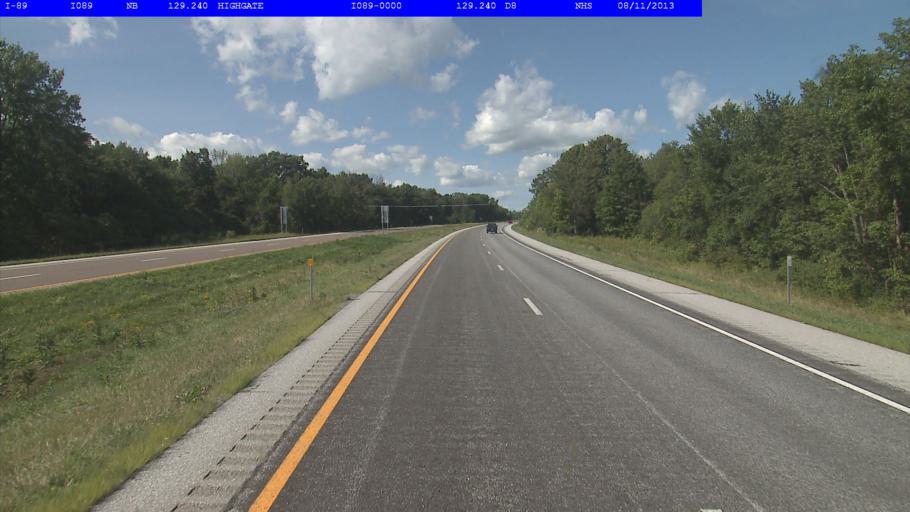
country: US
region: Vermont
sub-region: Franklin County
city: Swanton
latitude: 45.0009
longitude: -73.0867
